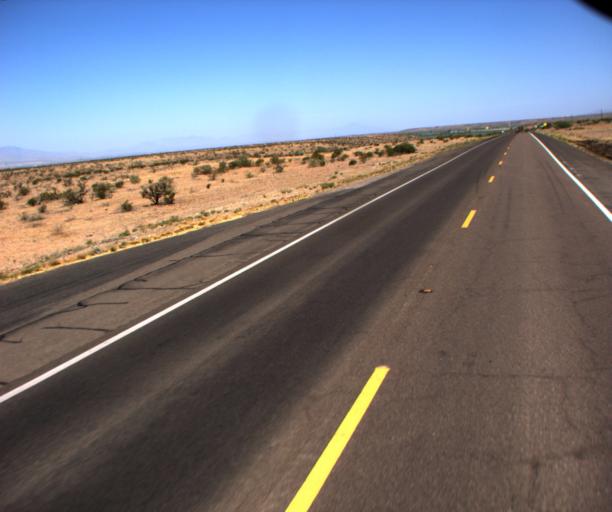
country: US
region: Arizona
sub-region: Graham County
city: Safford
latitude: 32.8079
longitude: -109.5843
